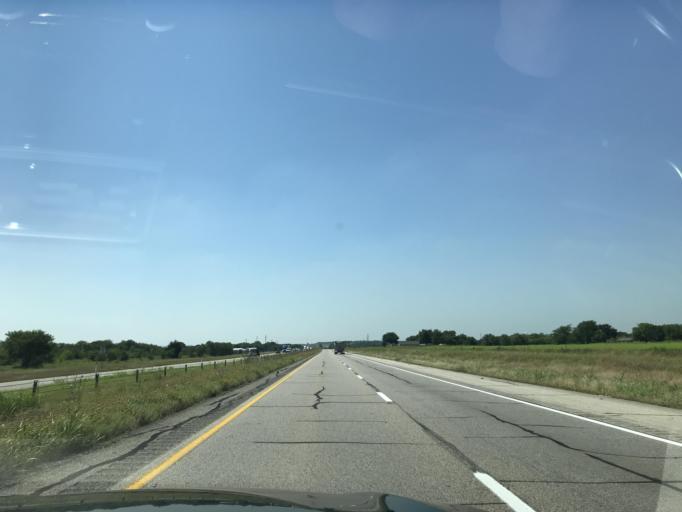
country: US
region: Texas
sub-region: Johnson County
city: Grandview
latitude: 32.3090
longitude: -97.1829
